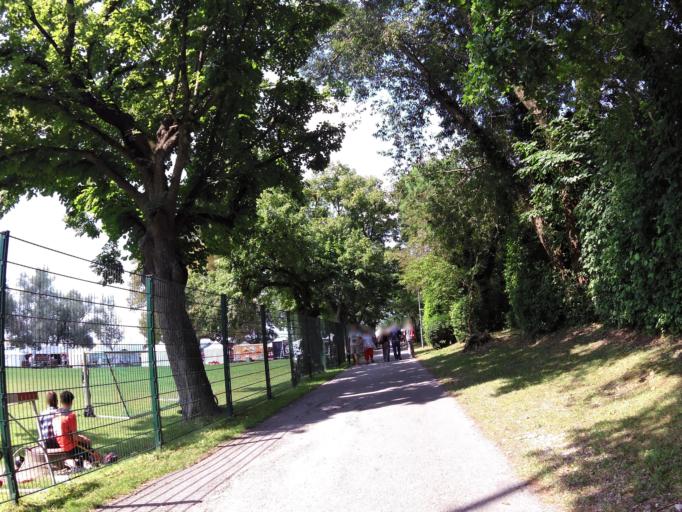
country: DE
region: Bavaria
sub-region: Upper Bavaria
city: Herrsching am Ammersee
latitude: 48.0025
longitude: 11.1687
